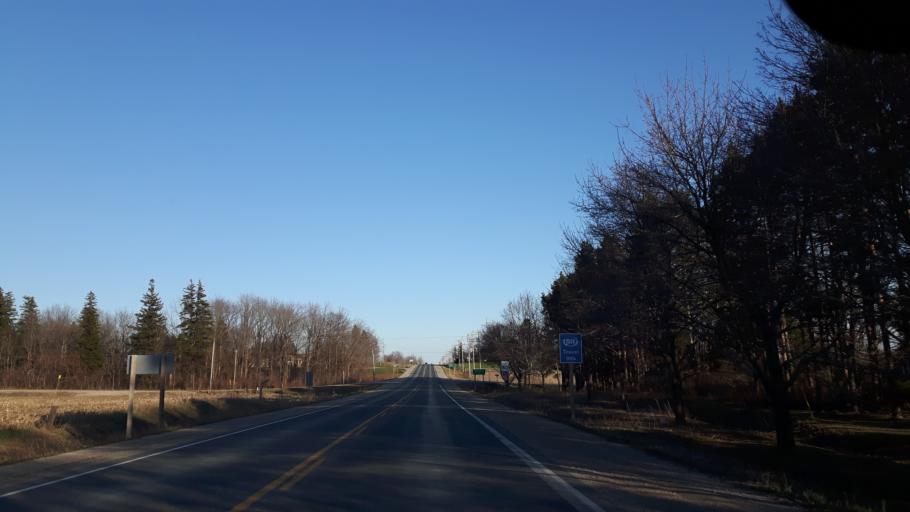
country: CA
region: Ontario
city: Goderich
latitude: 43.7251
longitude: -81.6818
